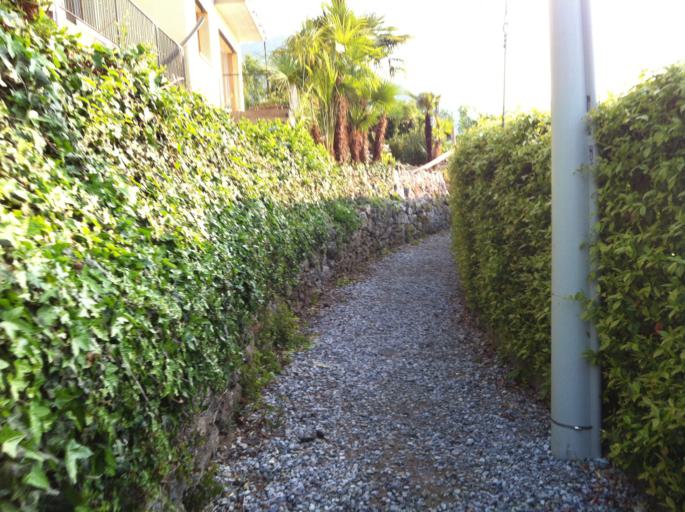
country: IT
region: Lombardy
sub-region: Provincia di Como
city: Menaggio
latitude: 46.0286
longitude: 9.2355
